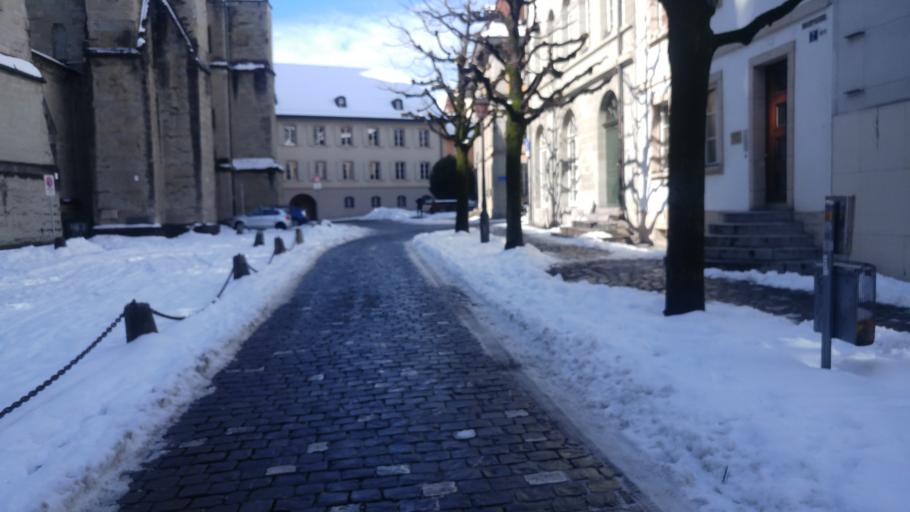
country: CH
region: Vaud
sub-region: Lausanne District
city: Lausanne
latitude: 46.5227
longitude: 6.6357
